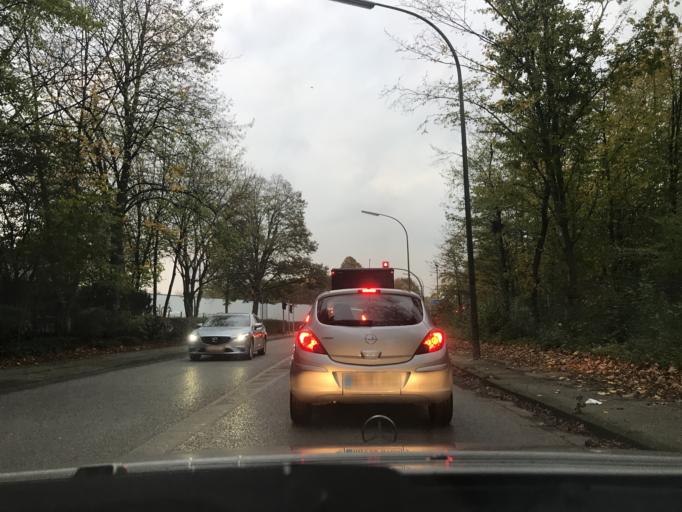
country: DE
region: North Rhine-Westphalia
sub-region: Regierungsbezirk Munster
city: Gelsenkirchen
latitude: 51.5357
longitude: 7.1272
